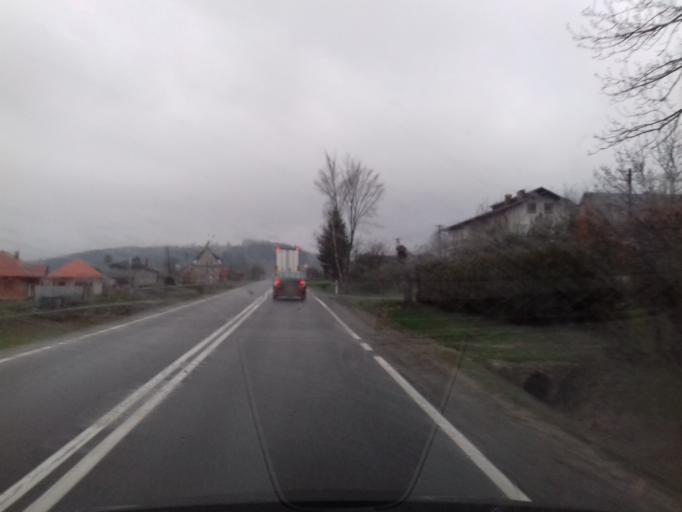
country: PL
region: Lesser Poland Voivodeship
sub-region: Powiat nowosadecki
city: Chelmiec
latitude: 49.6487
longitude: 20.6067
